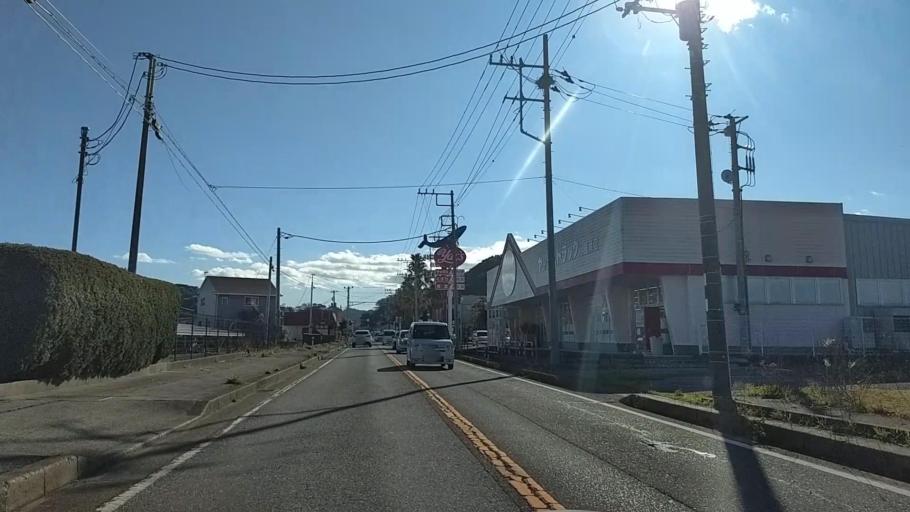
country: JP
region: Chiba
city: Tateyama
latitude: 35.1063
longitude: 139.8402
